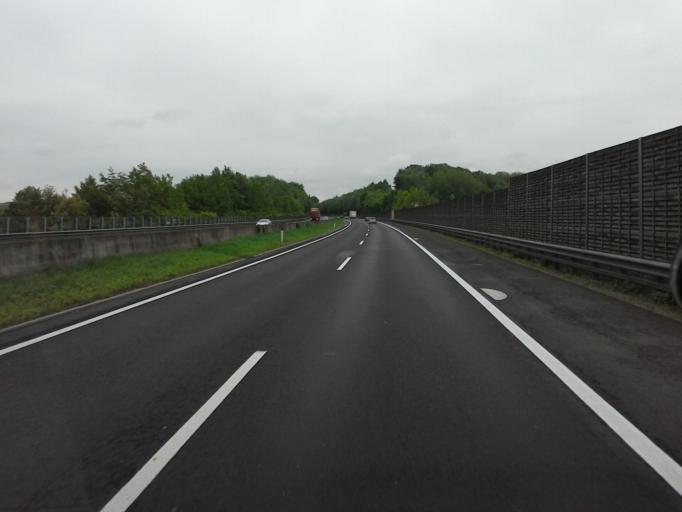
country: AT
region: Upper Austria
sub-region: Politischer Bezirk Scharding
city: Sankt Marienkirchen bei Schaerding
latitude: 48.3113
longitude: 13.4276
